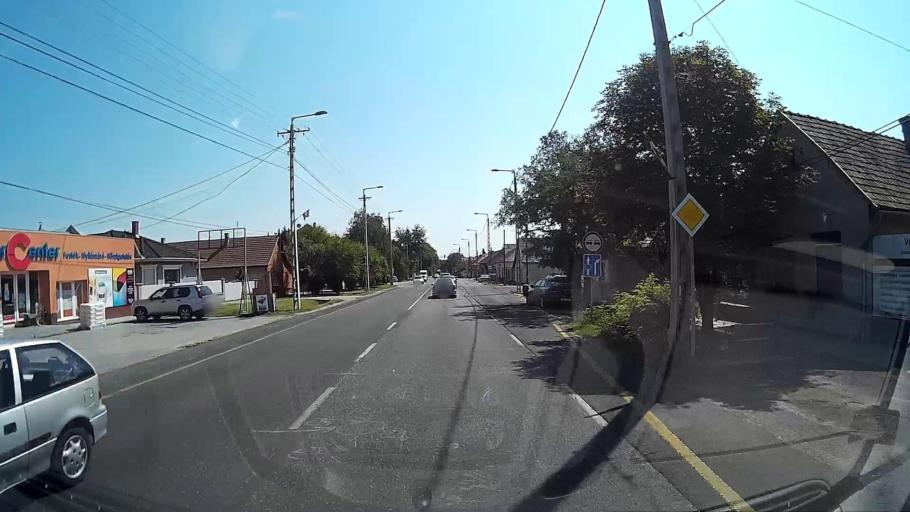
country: HU
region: Pest
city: Vecses
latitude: 47.4119
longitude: 19.2698
